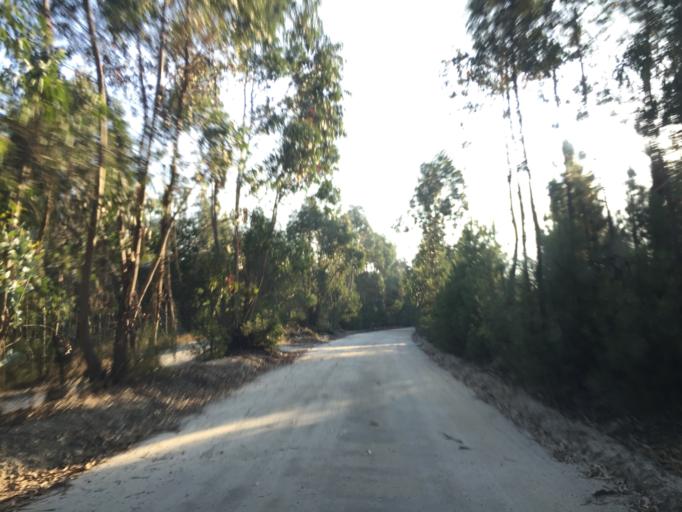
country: PT
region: Portalegre
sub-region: Ponte de Sor
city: Santo Andre
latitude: 39.1453
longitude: -8.3093
